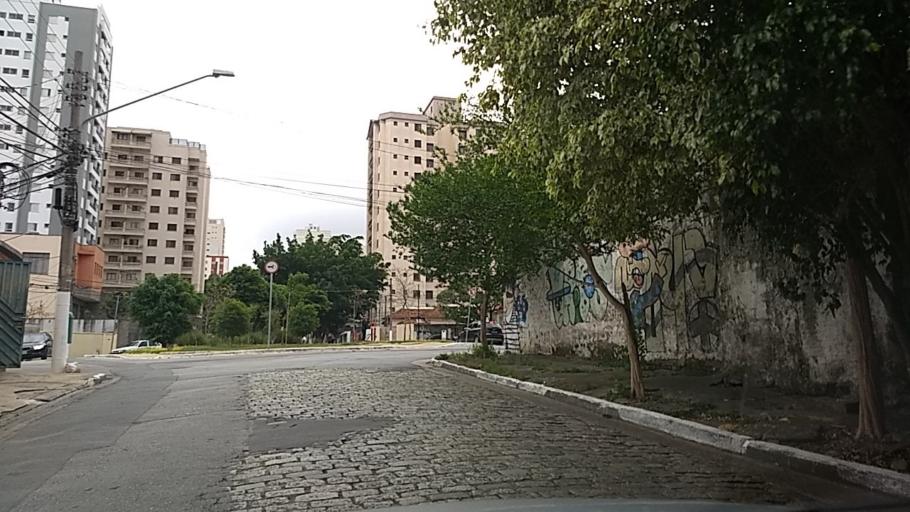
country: BR
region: Sao Paulo
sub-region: Sao Paulo
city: Sao Paulo
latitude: -23.6157
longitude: -46.6297
